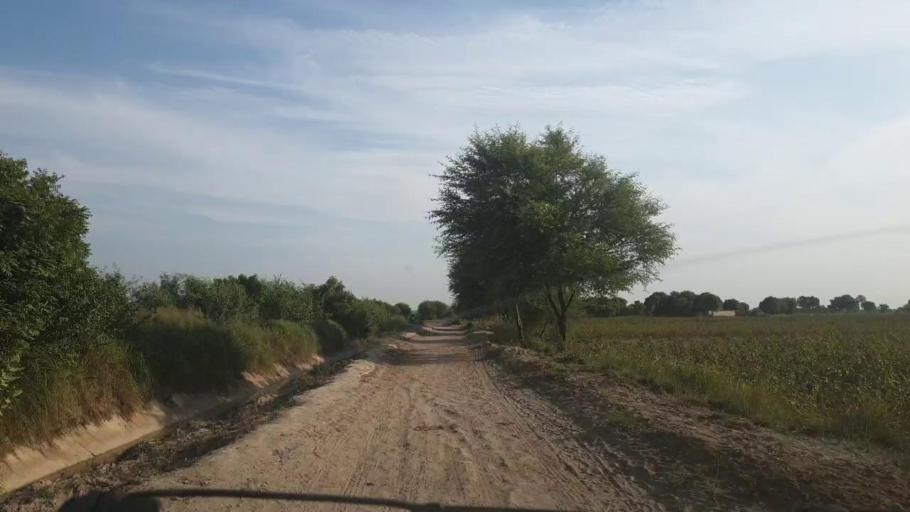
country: PK
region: Sindh
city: Tando Muhammad Khan
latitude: 25.2287
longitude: 68.5358
